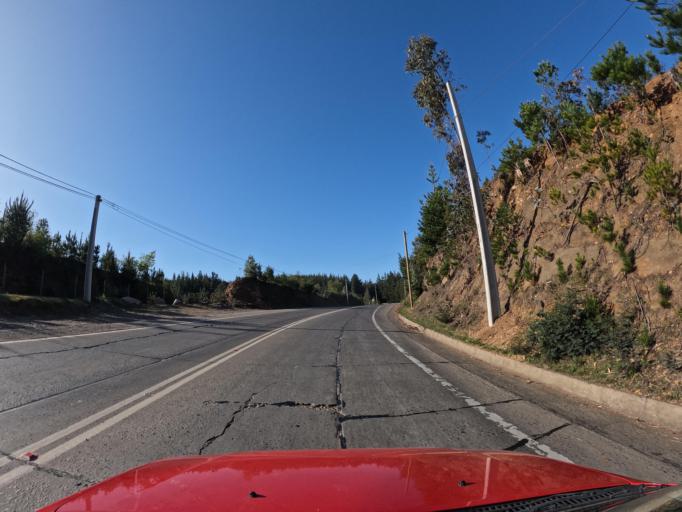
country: CL
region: Maule
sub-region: Provincia de Talca
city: Constitucion
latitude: -35.4381
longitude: -72.3358
